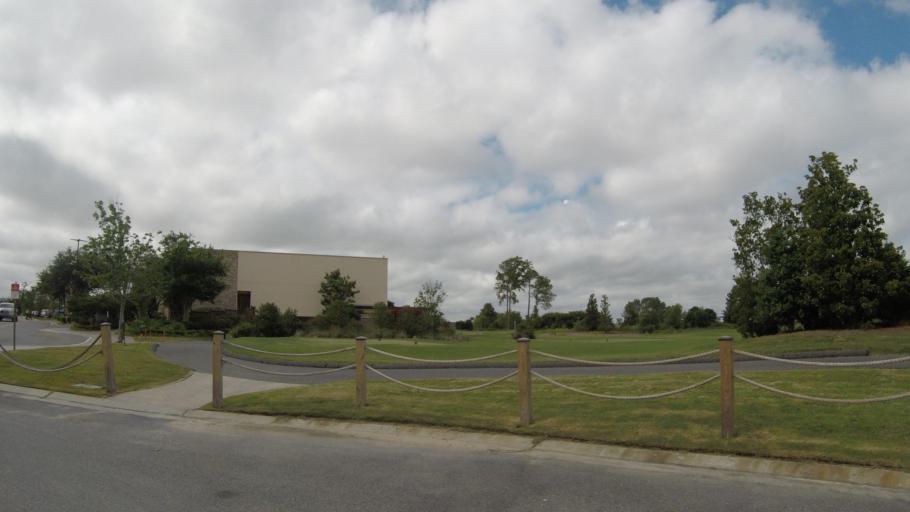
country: US
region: Louisiana
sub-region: Calcasieu Parish
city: Prien
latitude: 30.2042
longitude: -93.2666
